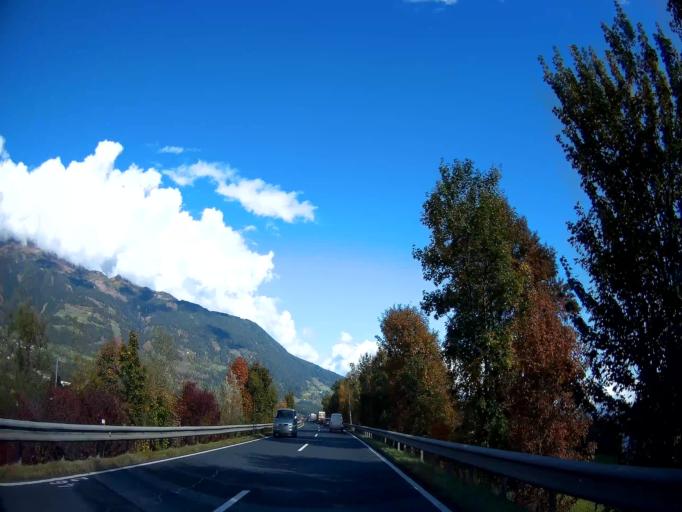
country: AT
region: Carinthia
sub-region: Politischer Bezirk Spittal an der Drau
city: Sachsenburg
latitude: 46.8284
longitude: 13.3740
